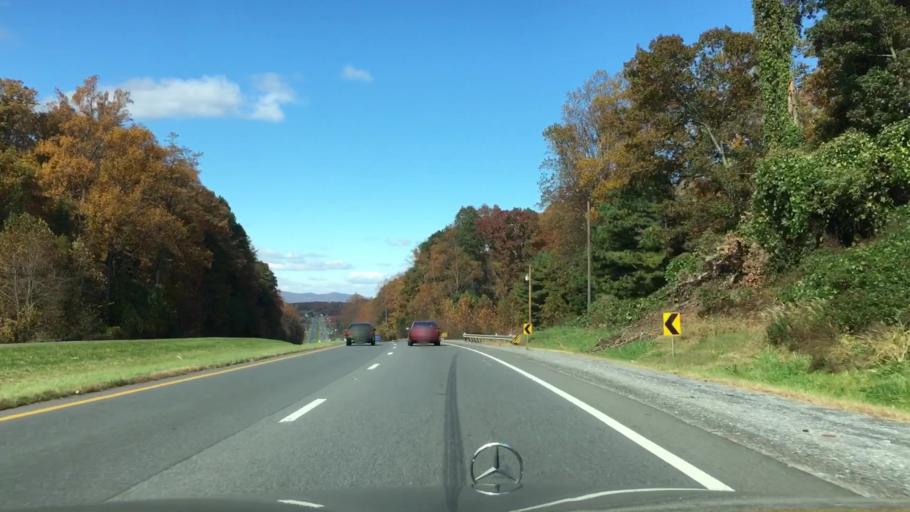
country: US
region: Virginia
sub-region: Campbell County
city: Rustburg
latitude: 37.2988
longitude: -79.1730
